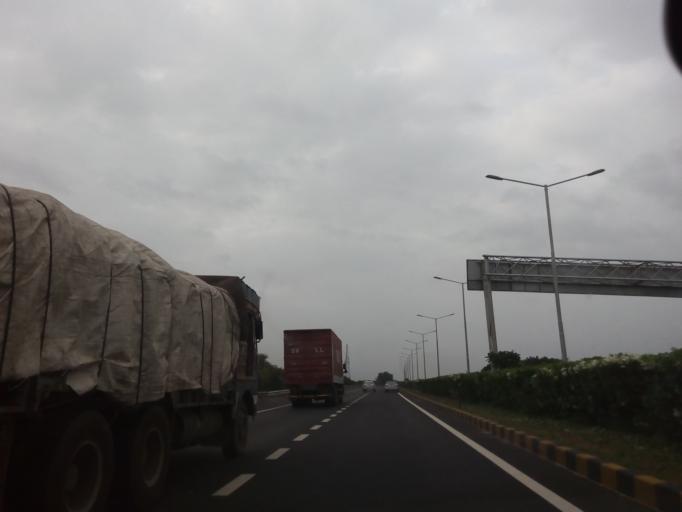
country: IN
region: Gujarat
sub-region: Kheda
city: Nadiad
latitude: 22.6925
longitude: 72.9010
